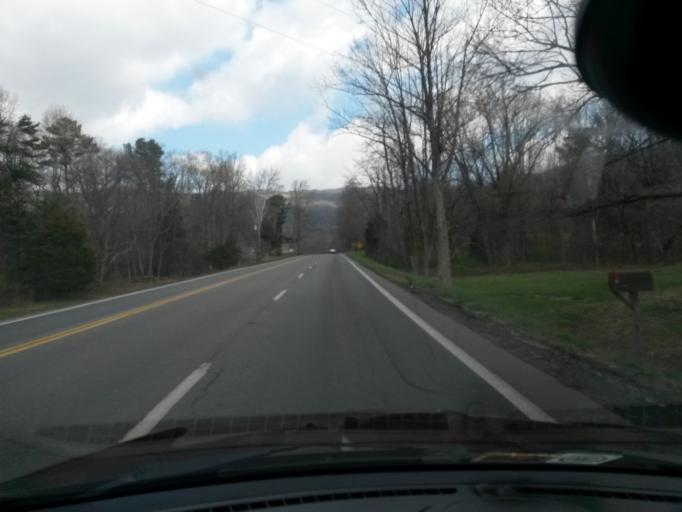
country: US
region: Virginia
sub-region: City of Waynesboro
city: Waynesboro
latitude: 38.0328
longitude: -78.8112
